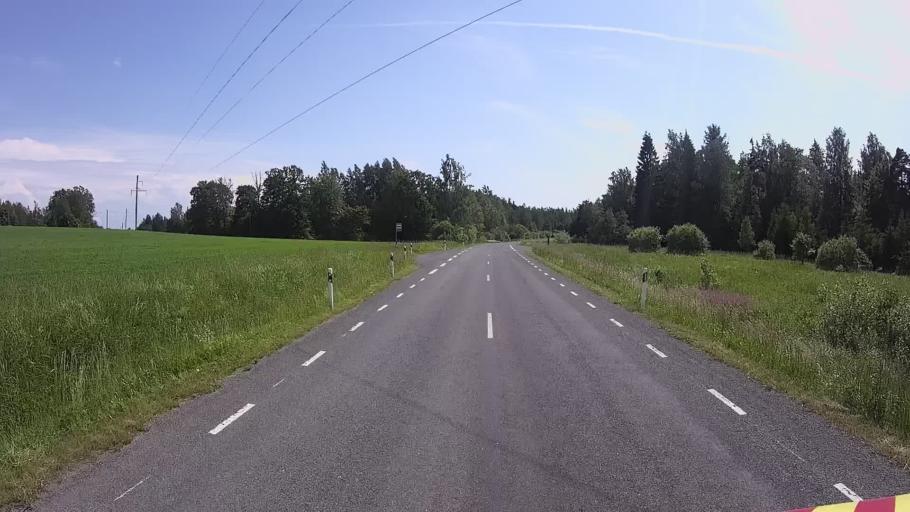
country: EE
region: Viljandimaa
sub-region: Karksi vald
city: Karksi-Nuia
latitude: 58.0894
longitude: 25.5580
